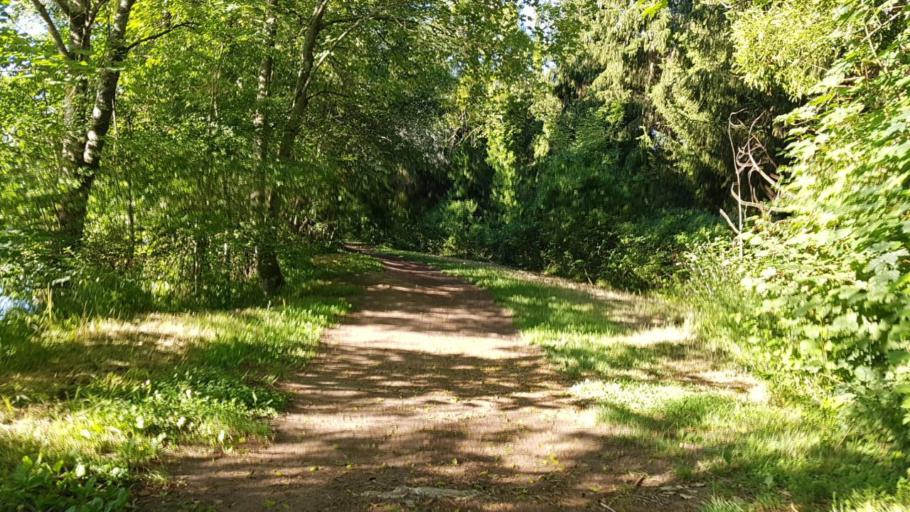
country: FR
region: Picardie
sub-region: Departement de l'Aisne
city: Essomes-sur-Marne
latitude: 49.0346
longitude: 3.3819
